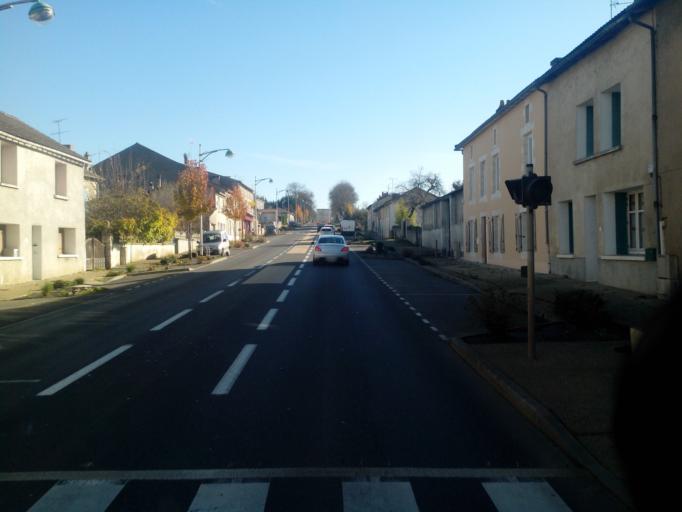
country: FR
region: Poitou-Charentes
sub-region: Departement de la Vienne
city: Terce
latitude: 46.4354
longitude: 0.5980
